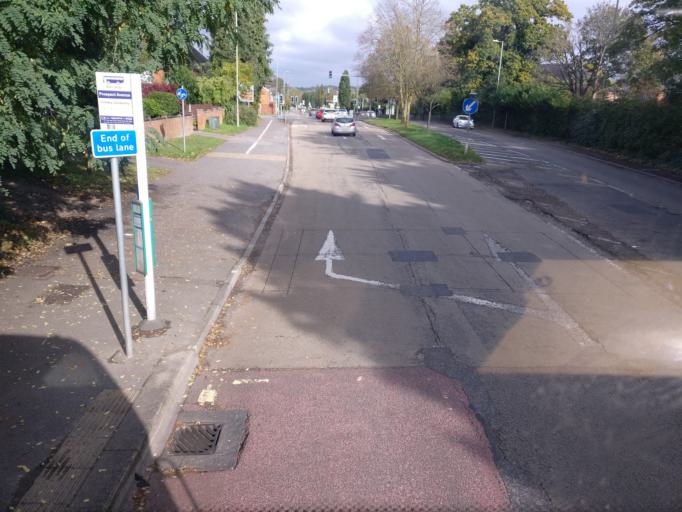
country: GB
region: England
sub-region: Hampshire
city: Farnborough
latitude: 51.3039
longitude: -0.7515
